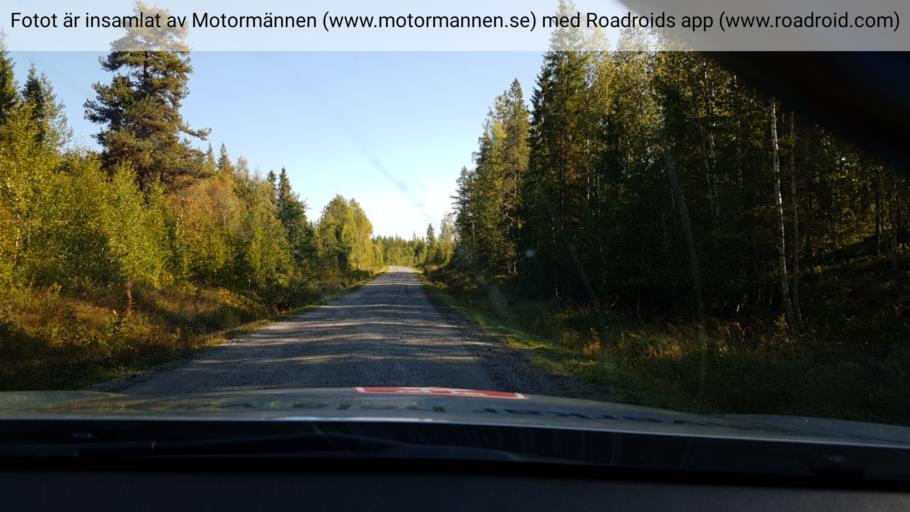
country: SE
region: Vaesterbotten
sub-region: Norsjo Kommun
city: Norsjoe
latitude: 64.6807
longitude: 19.3954
